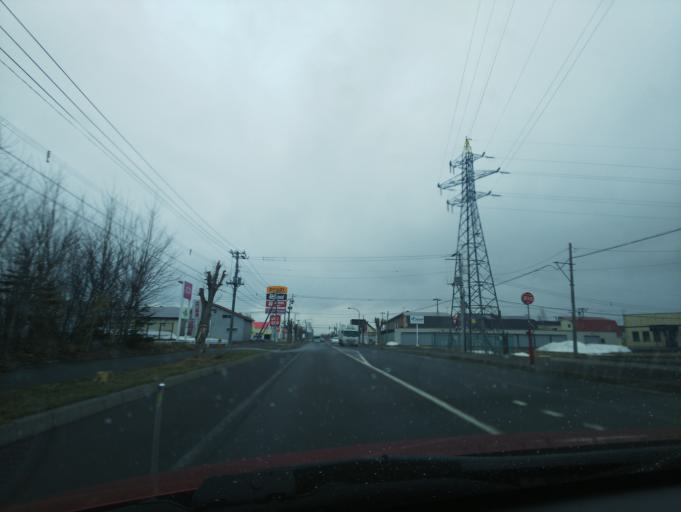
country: JP
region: Hokkaido
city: Nayoro
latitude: 44.3380
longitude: 142.4503
